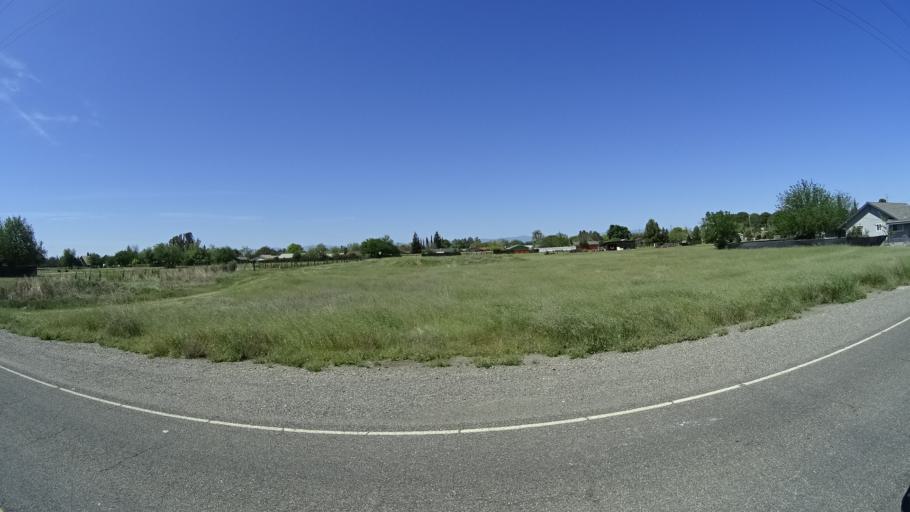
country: US
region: California
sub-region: Glenn County
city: Orland
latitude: 39.7384
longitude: -122.1781
